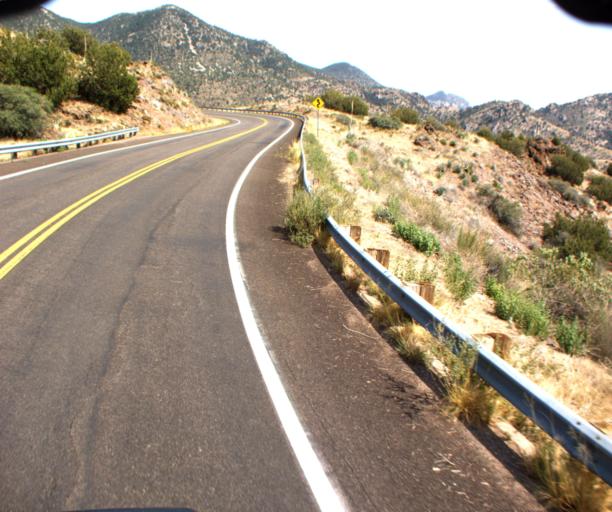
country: US
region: Arizona
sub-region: Greenlee County
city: Clifton
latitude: 33.0484
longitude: -109.1006
